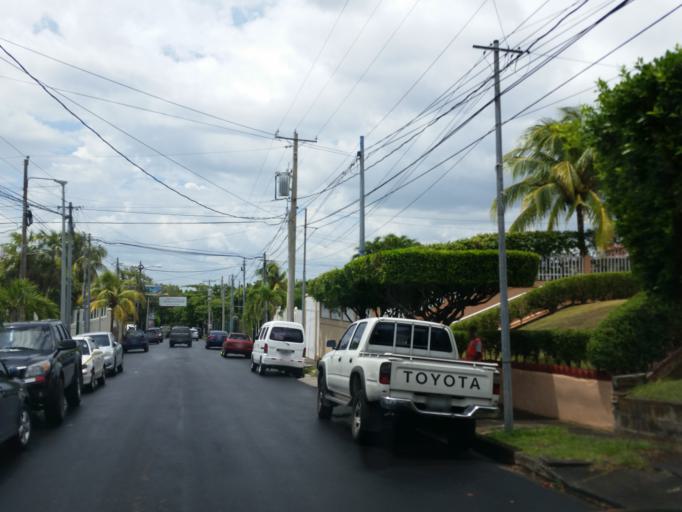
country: NI
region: Managua
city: Managua
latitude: 12.1135
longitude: -86.2634
